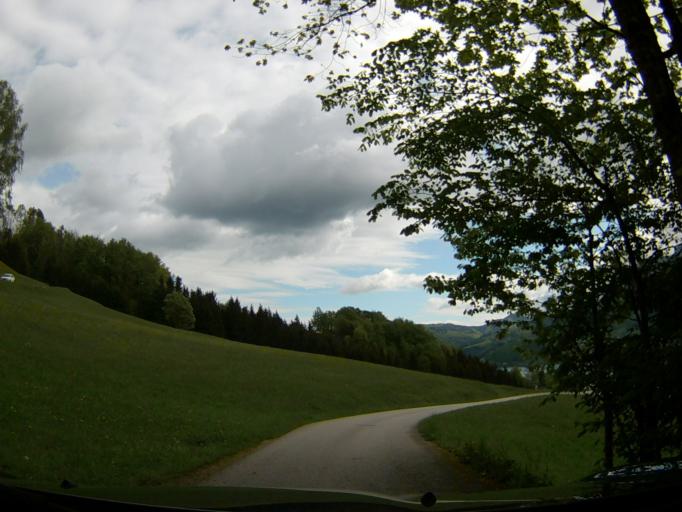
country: AT
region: Upper Austria
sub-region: Politischer Bezirk Vocklabruck
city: Steinbach am Attersee
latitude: 47.8241
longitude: 13.5036
